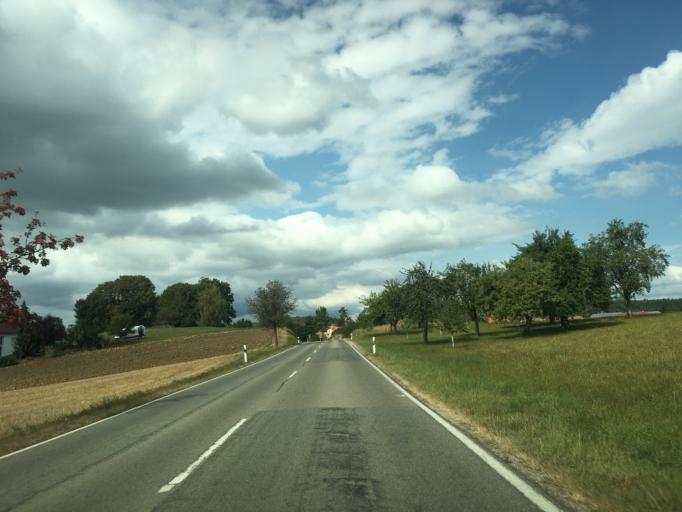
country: DE
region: Baden-Wuerttemberg
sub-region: Tuebingen Region
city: Gomadingen
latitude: 48.3528
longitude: 9.3408
